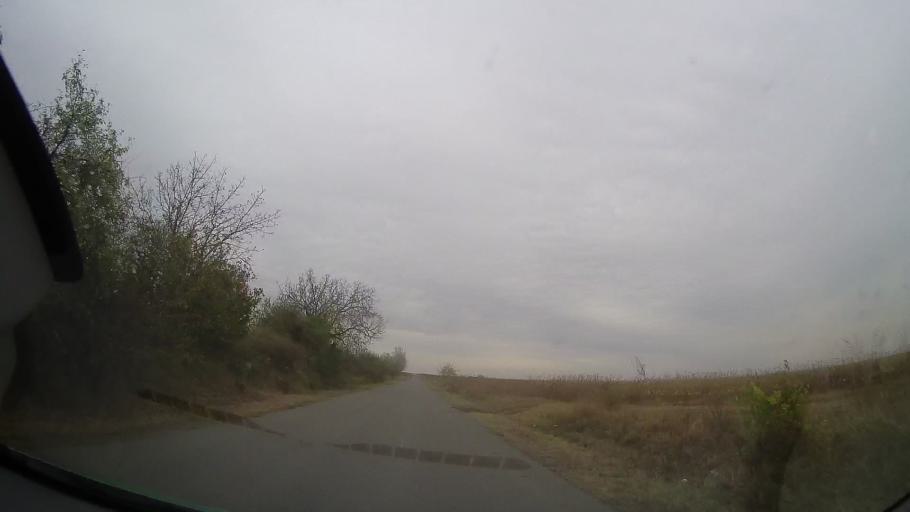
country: RO
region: Prahova
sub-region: Comuna Ceptura
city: Ceptura de Jos
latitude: 45.0140
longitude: 26.3439
